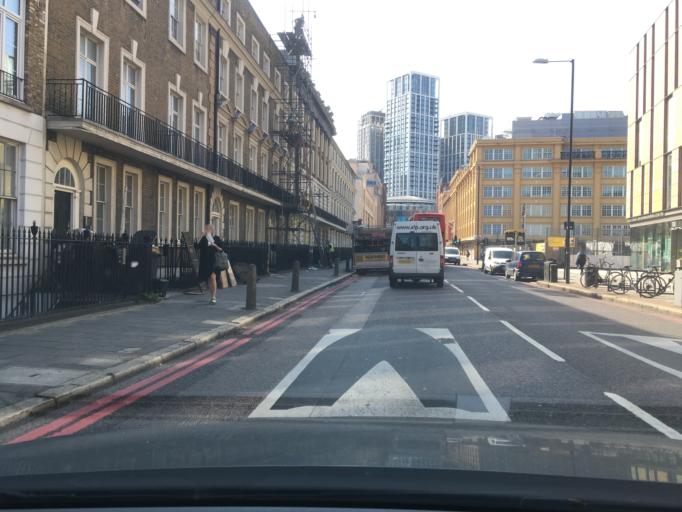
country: GB
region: England
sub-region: Greater London
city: City of Westminster
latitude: 51.5061
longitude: -0.1101
